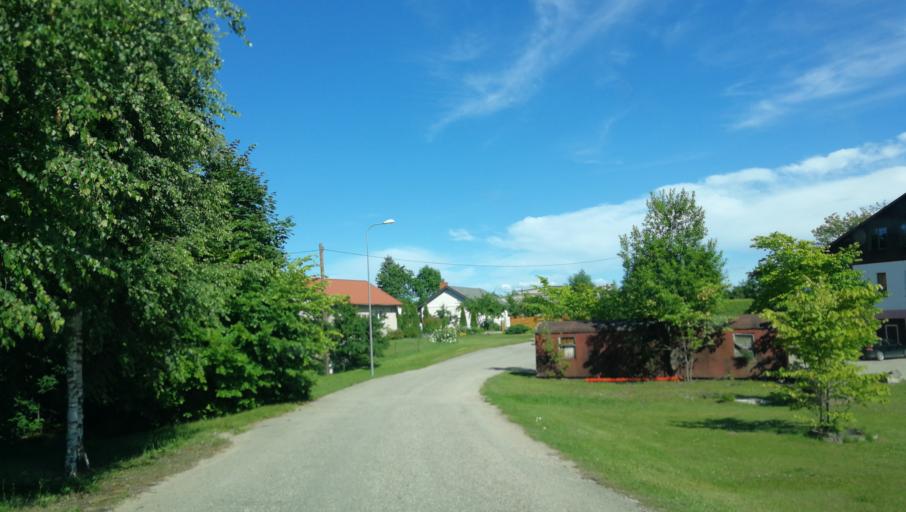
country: LV
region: Cesvaine
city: Cesvaine
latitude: 56.9694
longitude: 26.3155
